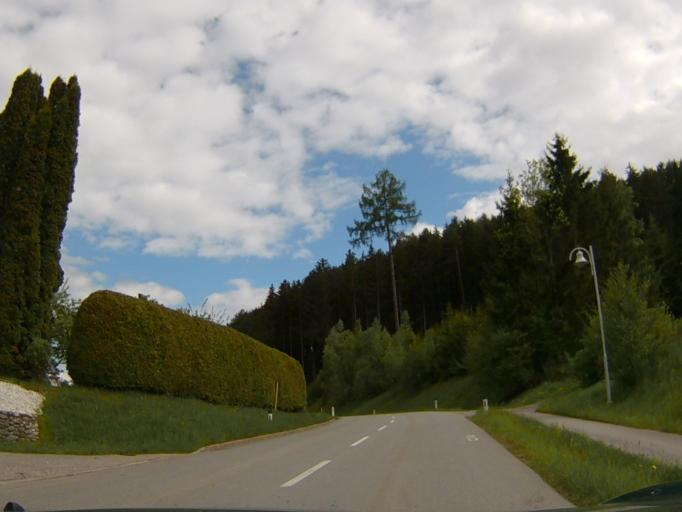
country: AT
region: Carinthia
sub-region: Politischer Bezirk Villach Land
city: Stockenboi
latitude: 46.7377
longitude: 13.5797
